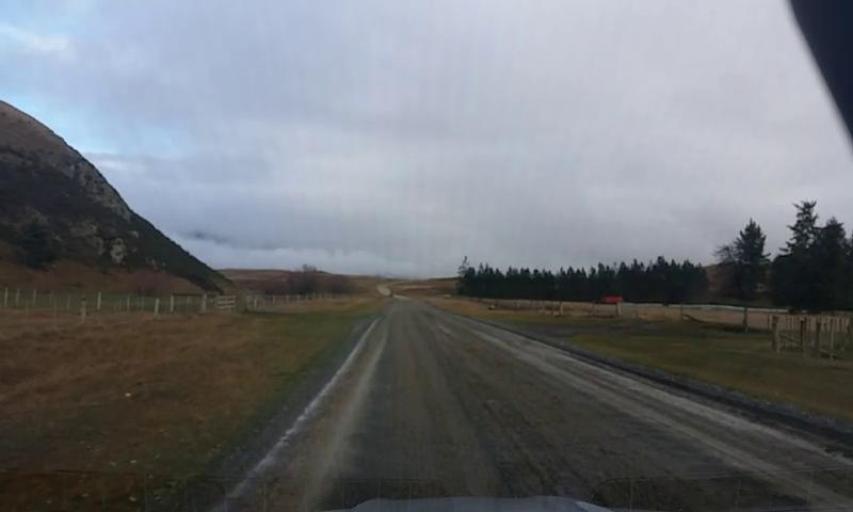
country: NZ
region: Canterbury
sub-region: Ashburton District
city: Methven
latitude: -43.6146
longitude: 171.1667
